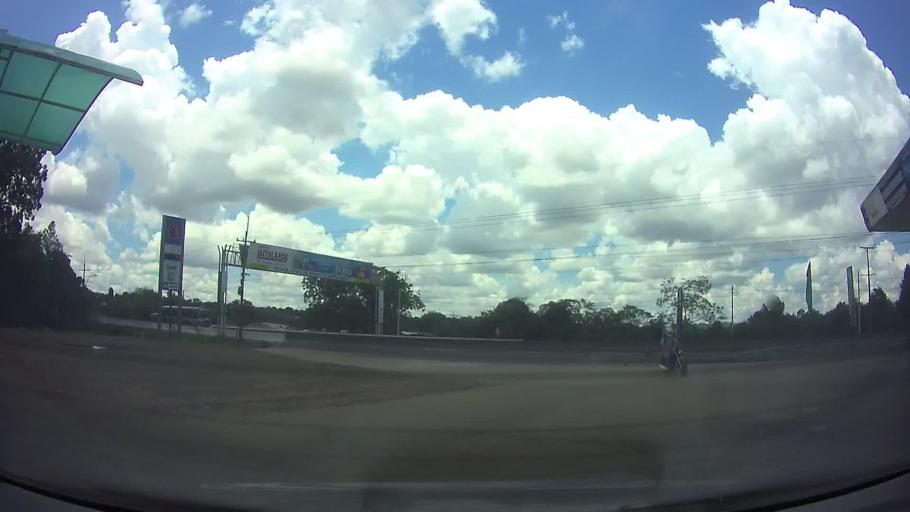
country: PY
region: Central
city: Capiata
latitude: -25.3772
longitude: -57.4015
